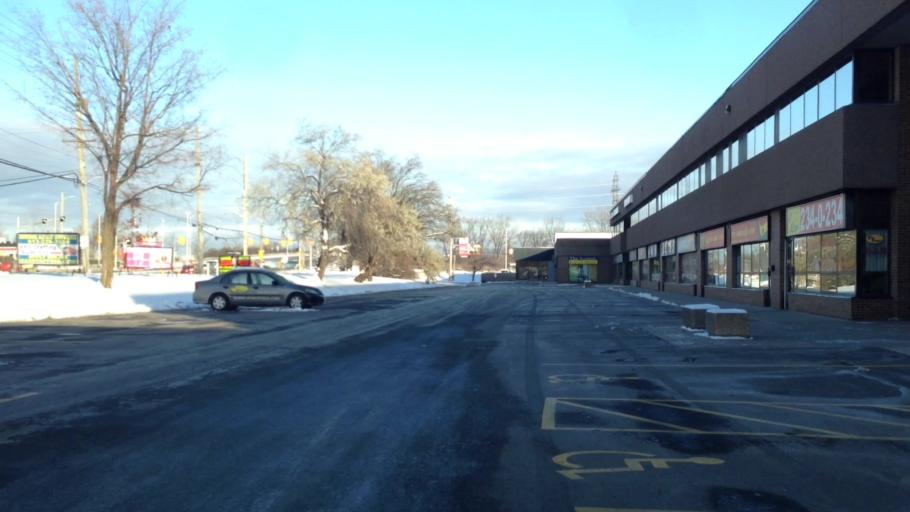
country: CA
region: Ontario
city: Ottawa
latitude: 45.4051
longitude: -75.6260
